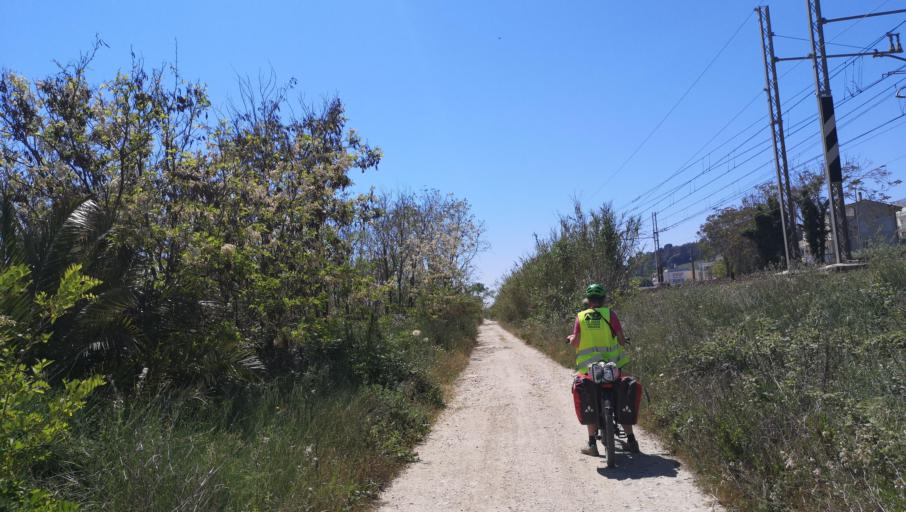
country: IT
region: The Marches
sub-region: Province of Fermo
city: Campofilone
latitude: 43.0607
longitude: 13.8499
